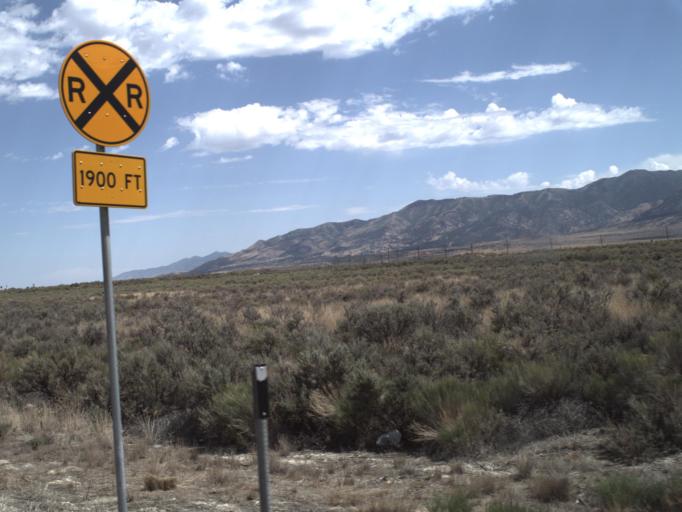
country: US
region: Utah
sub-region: Tooele County
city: Tooele
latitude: 40.3600
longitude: -112.4139
